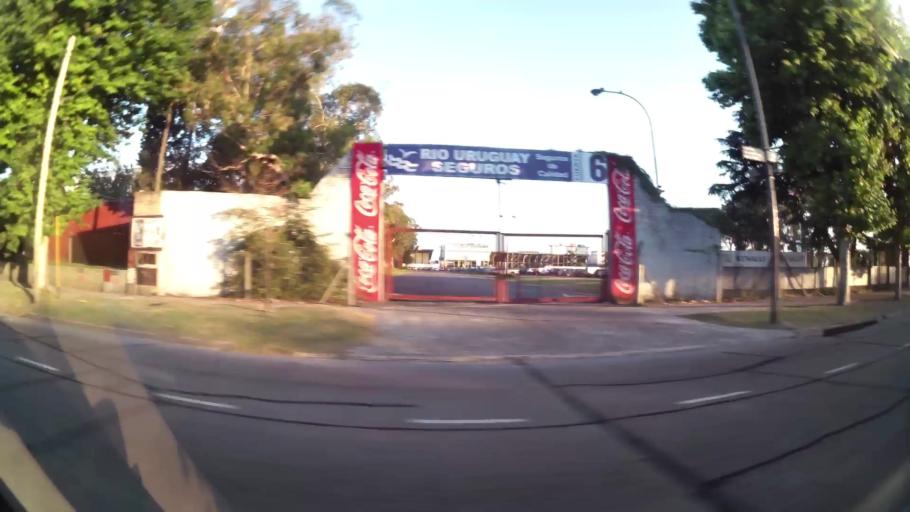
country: AR
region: Buenos Aires F.D.
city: Villa Lugano
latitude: -34.6933
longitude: -58.4646
